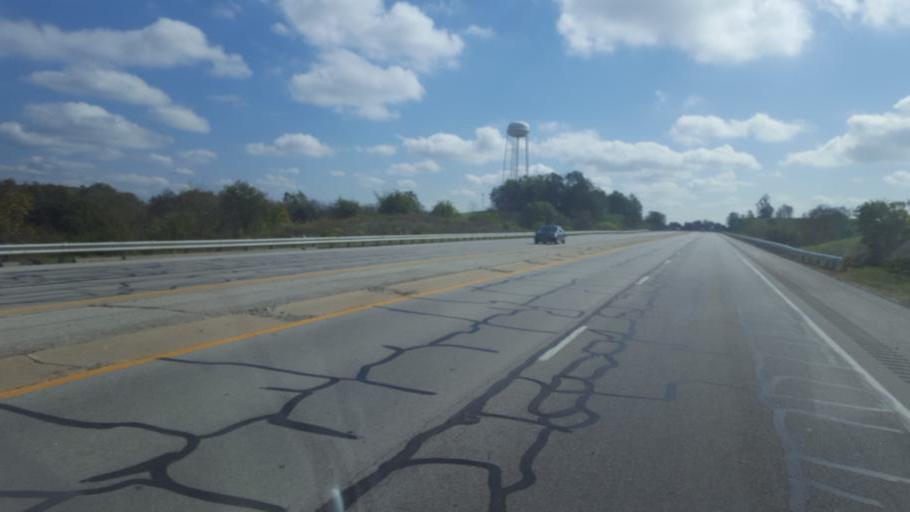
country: US
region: Kentucky
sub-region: Mason County
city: Maysville
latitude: 38.6100
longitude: -83.7713
